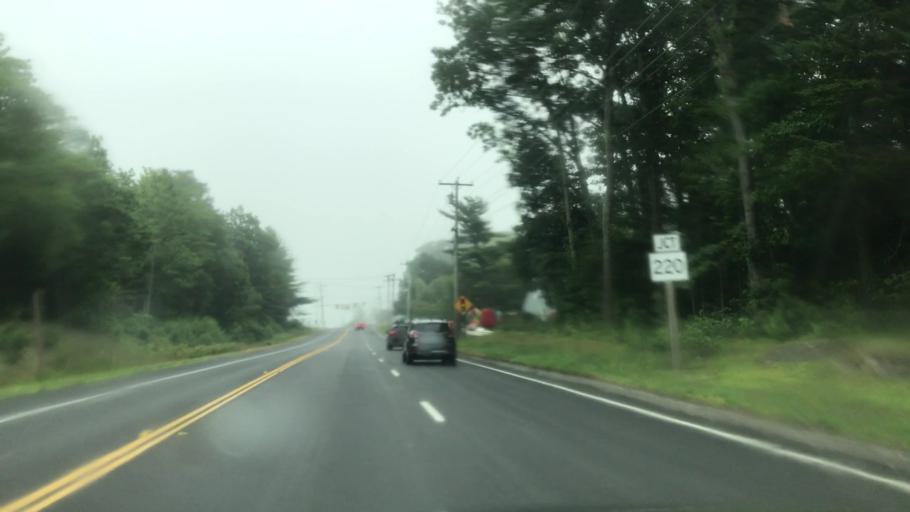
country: US
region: Maine
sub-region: Lincoln County
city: Waldoboro
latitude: 44.1031
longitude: -69.3722
